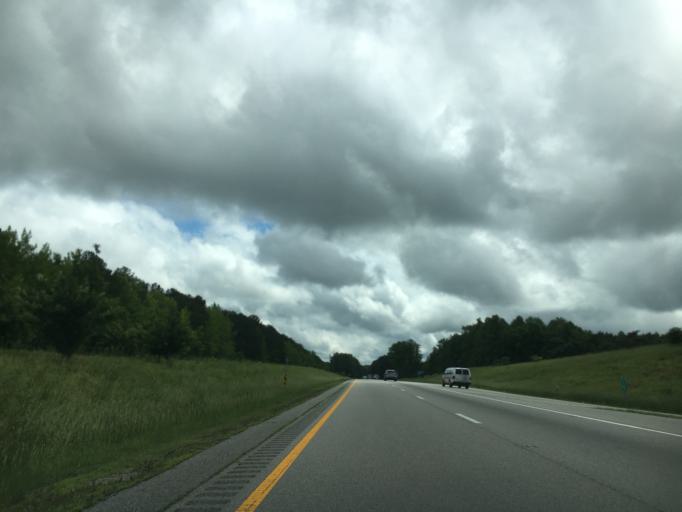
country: US
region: Virginia
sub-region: Mecklenburg County
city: South Hill
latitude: 36.7479
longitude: -78.0964
